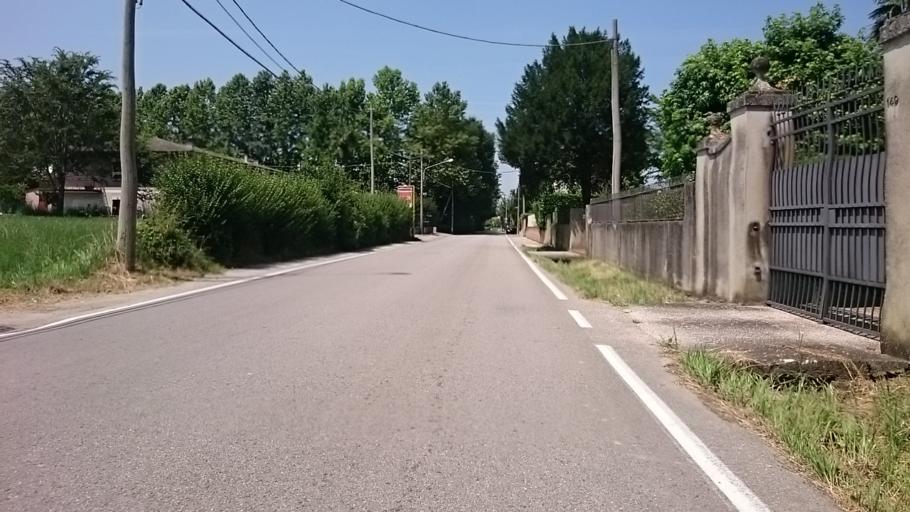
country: IT
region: Veneto
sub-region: Provincia di Vicenza
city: Vicenza
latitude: 45.5364
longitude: 11.5683
